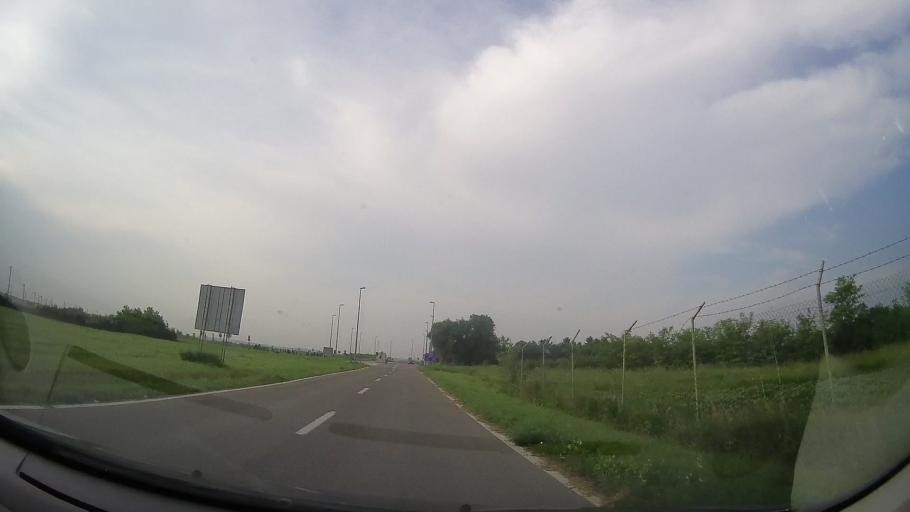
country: RS
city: Jasa Tomic
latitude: 45.4723
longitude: 20.8490
